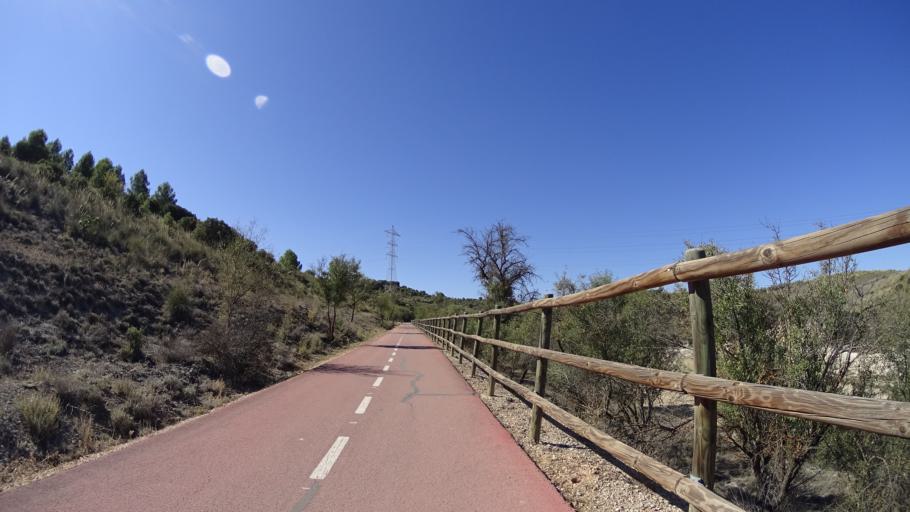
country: ES
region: Madrid
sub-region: Provincia de Madrid
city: Arganda
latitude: 40.2697
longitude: -3.4592
